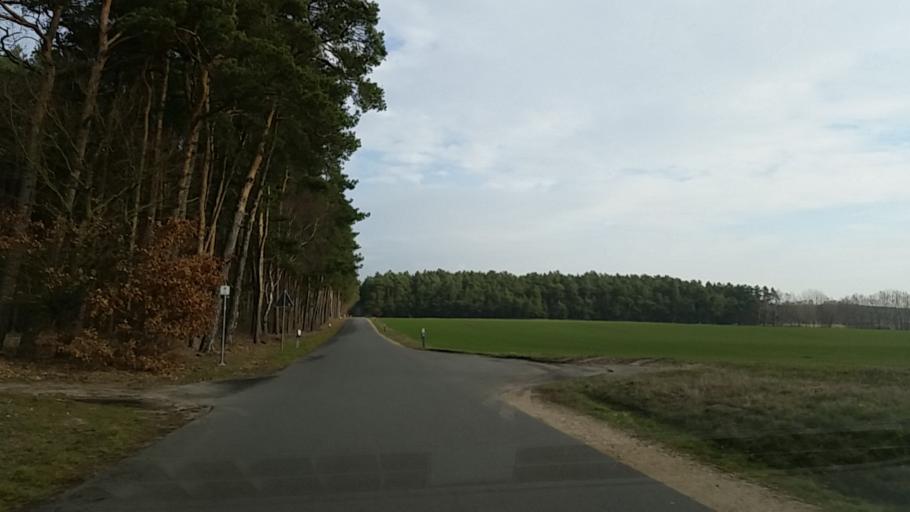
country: DE
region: Lower Saxony
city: Soltendieck
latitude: 52.8356
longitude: 10.7485
